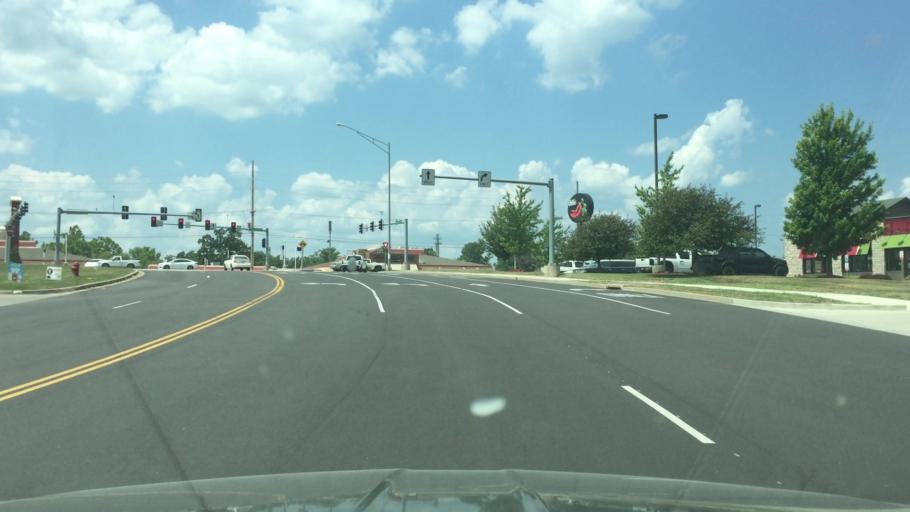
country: US
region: Missouri
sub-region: Miller County
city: Lake Ozark
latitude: 38.1620
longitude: -92.6064
